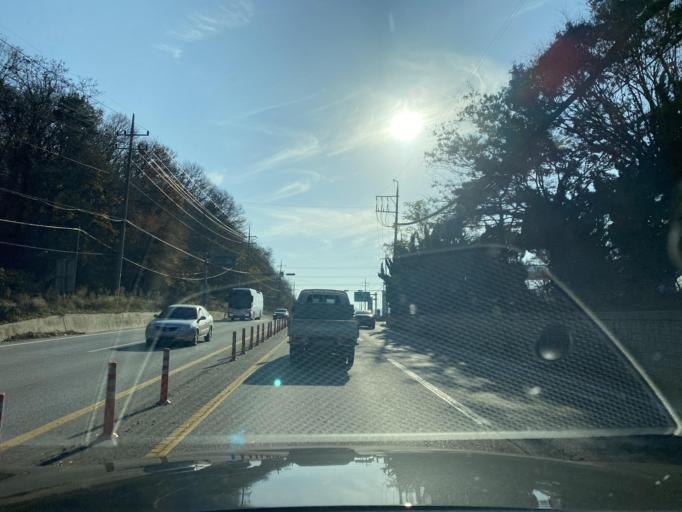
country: KR
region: Chungcheongnam-do
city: Asan
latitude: 36.7687
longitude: 126.9266
